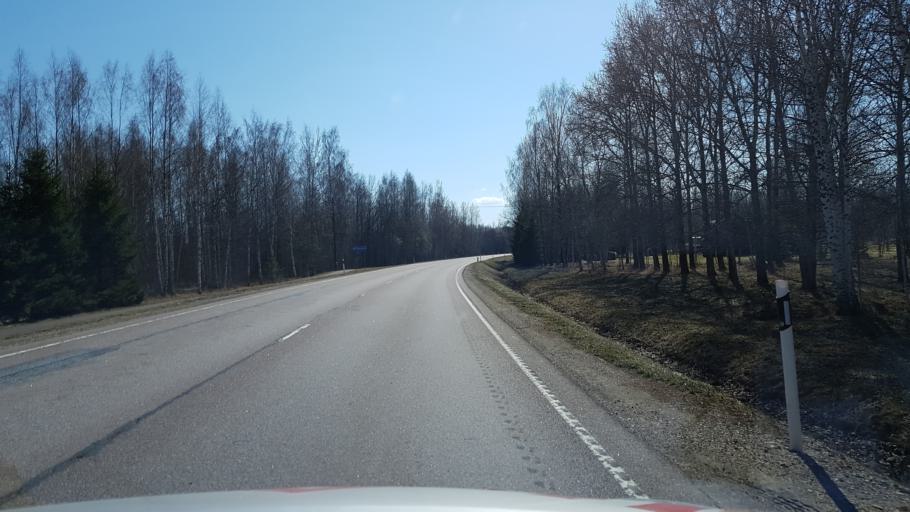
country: EE
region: Jogevamaa
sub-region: Mustvee linn
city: Mustvee
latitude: 58.7898
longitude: 26.9428
